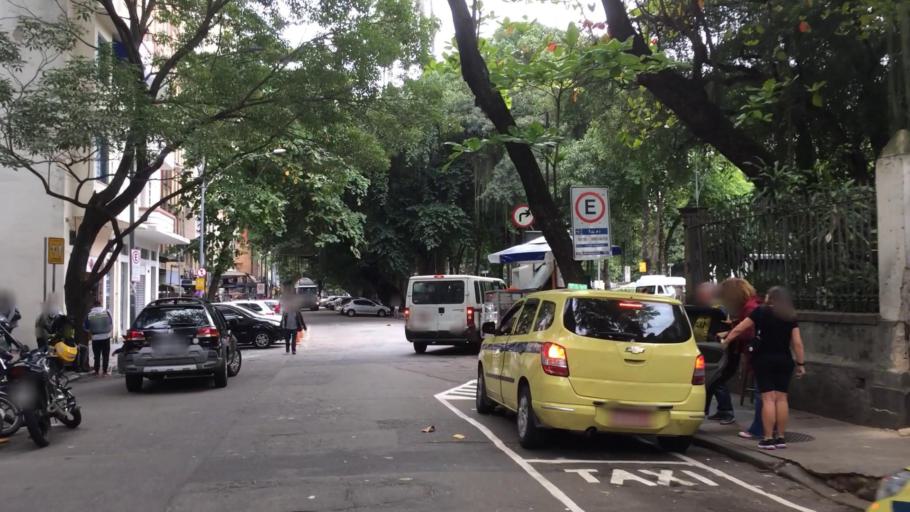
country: BR
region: Rio de Janeiro
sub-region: Rio De Janeiro
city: Rio de Janeiro
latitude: -22.9310
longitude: -43.1798
